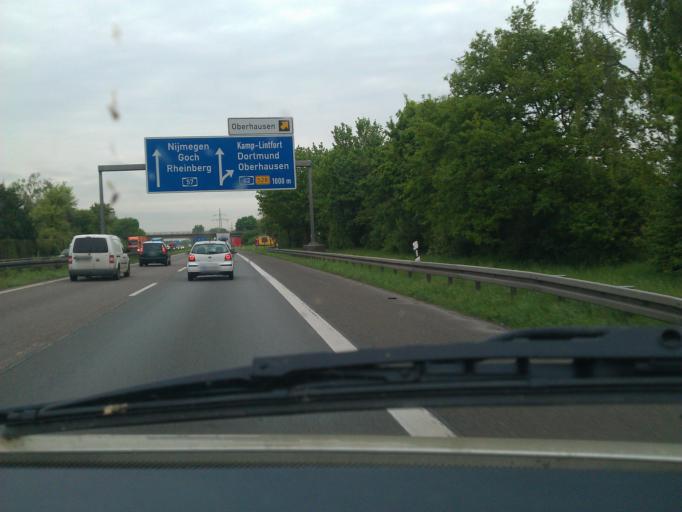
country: DE
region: North Rhine-Westphalia
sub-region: Regierungsbezirk Dusseldorf
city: Moers
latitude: 51.4741
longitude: 6.5866
